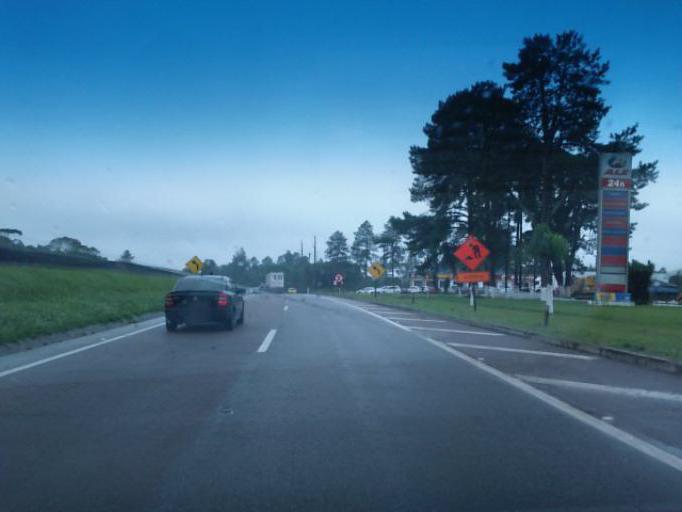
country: BR
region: Parana
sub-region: Sao Jose Dos Pinhais
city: Sao Jose dos Pinhais
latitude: -25.7784
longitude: -49.1202
